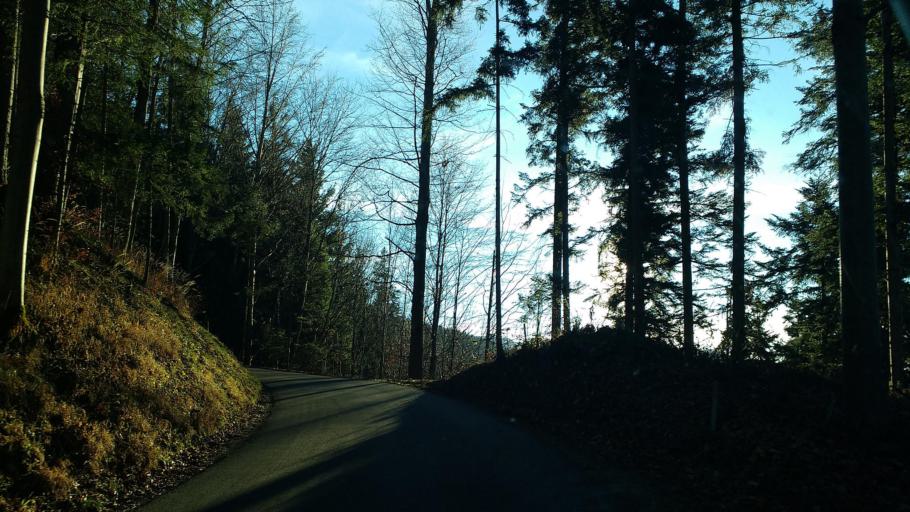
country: AT
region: Upper Austria
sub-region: Politischer Bezirk Kirchdorf an der Krems
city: Micheldorf in Oberoesterreich
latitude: 47.9101
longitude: 14.1469
